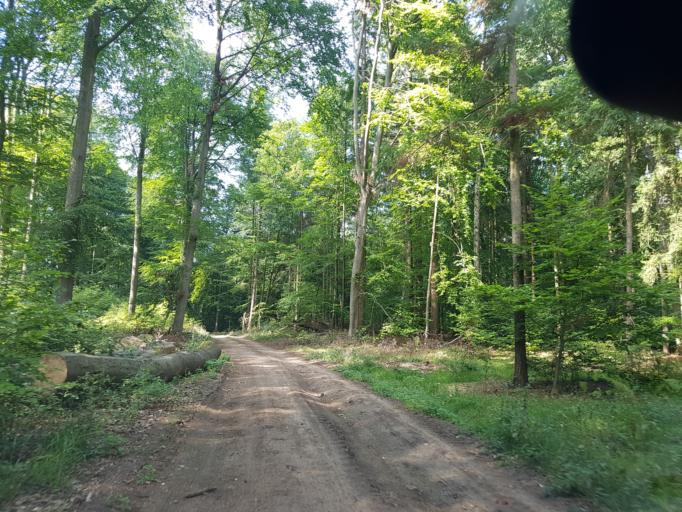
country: DE
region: Brandenburg
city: Gorzke
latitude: 52.0731
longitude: 12.3619
